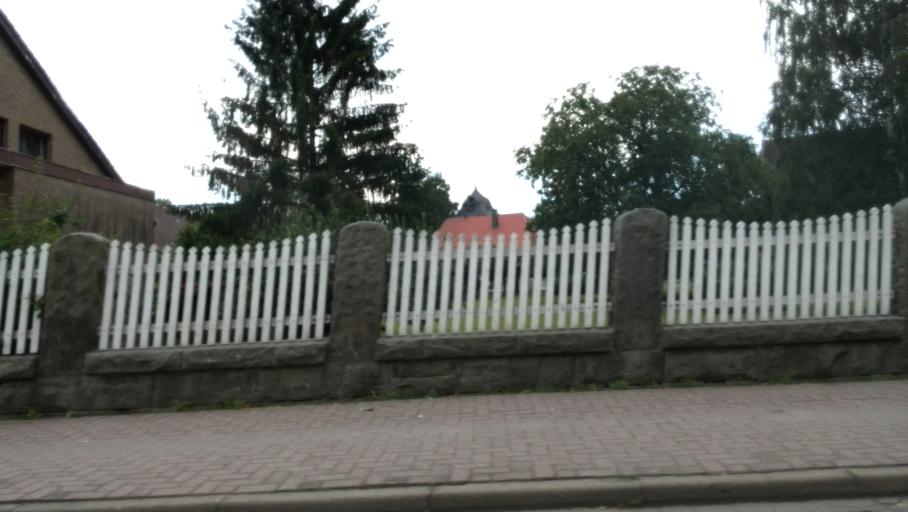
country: DE
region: Lower Saxony
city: Holle
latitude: 52.0884
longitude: 10.1579
